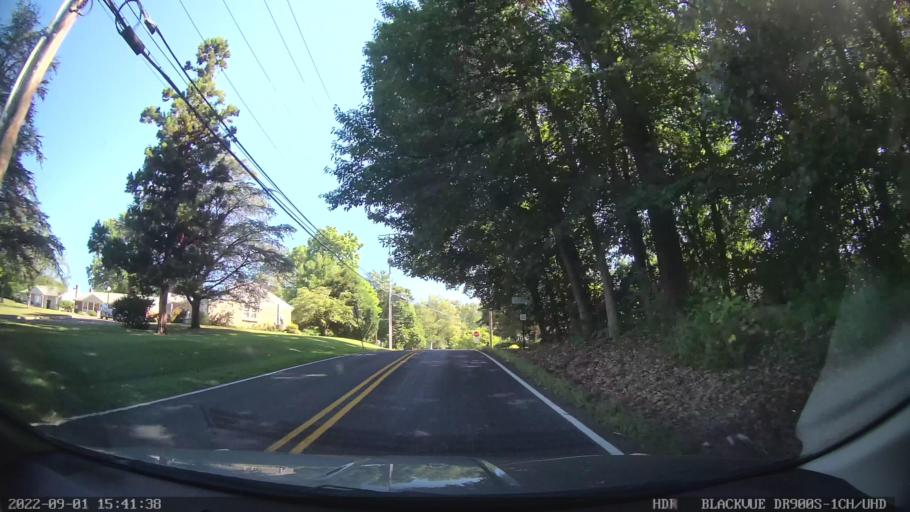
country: US
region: Pennsylvania
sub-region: Berks County
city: Topton
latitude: 40.4958
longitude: -75.7010
